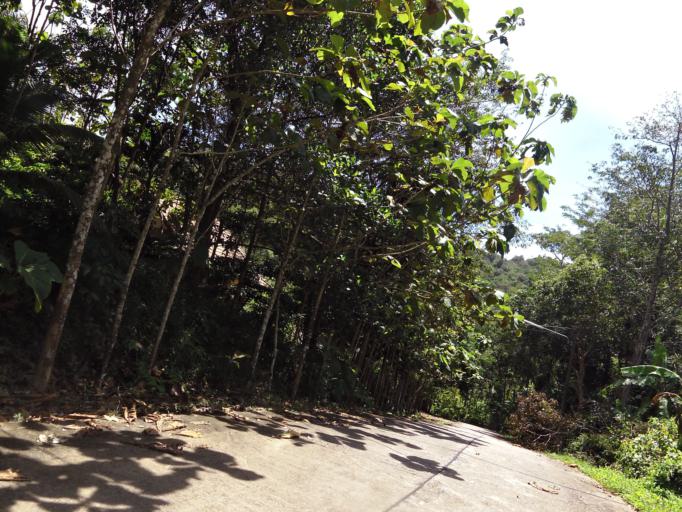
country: TH
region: Phuket
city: Ban Karon
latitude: 7.8470
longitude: 98.3066
